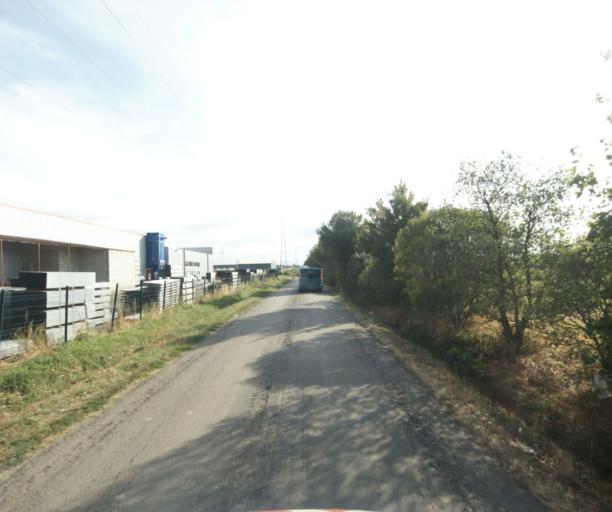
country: FR
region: Midi-Pyrenees
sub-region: Departement de la Haute-Garonne
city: Revel
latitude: 43.4594
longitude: 1.9788
